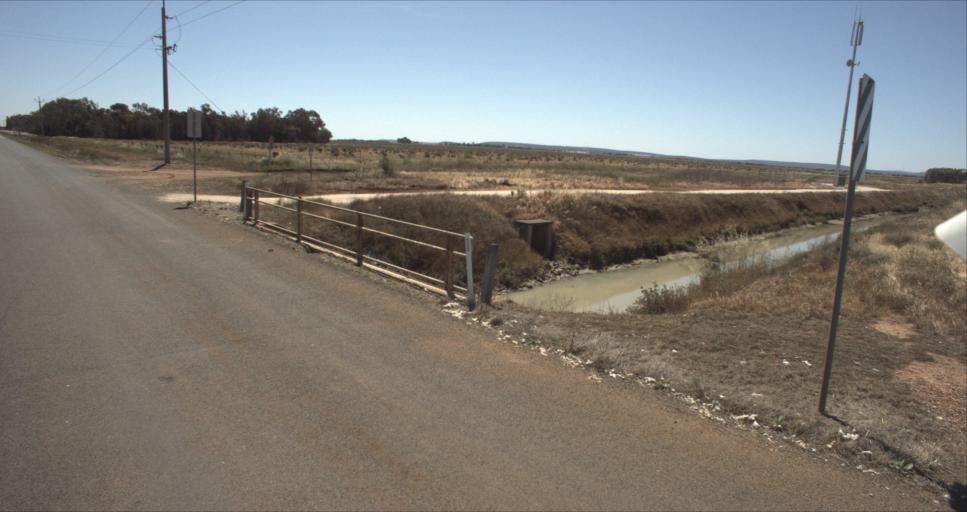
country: AU
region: New South Wales
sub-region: Leeton
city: Leeton
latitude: -34.4738
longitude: 146.2918
